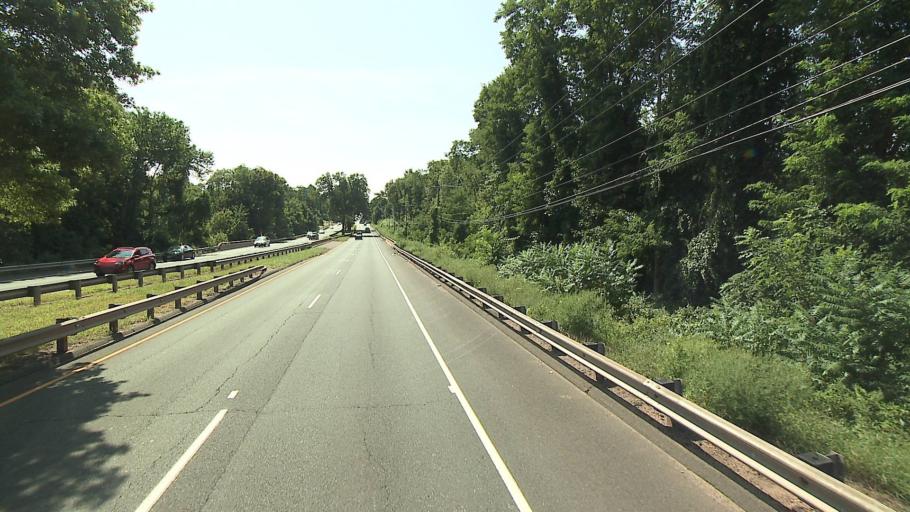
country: US
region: Connecticut
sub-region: Hartford County
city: Windsor
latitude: 41.8626
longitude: -72.6039
